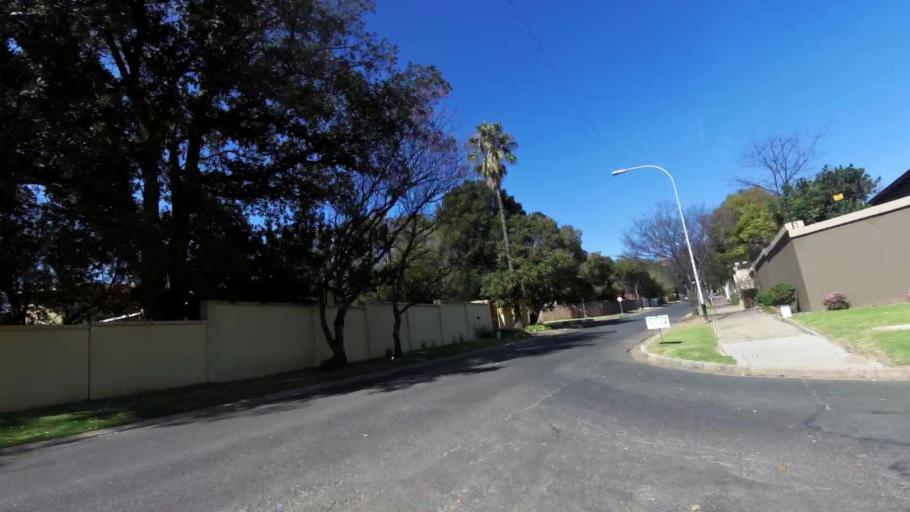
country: ZA
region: Gauteng
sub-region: City of Johannesburg Metropolitan Municipality
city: Roodepoort
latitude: -26.1455
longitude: 27.9458
